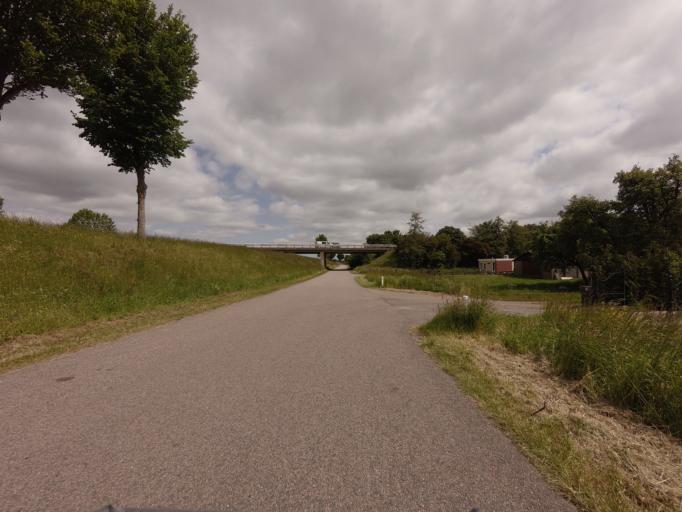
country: NL
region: North Holland
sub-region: Gemeente Beemster
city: Halfweg
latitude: 52.5510
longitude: 4.8496
